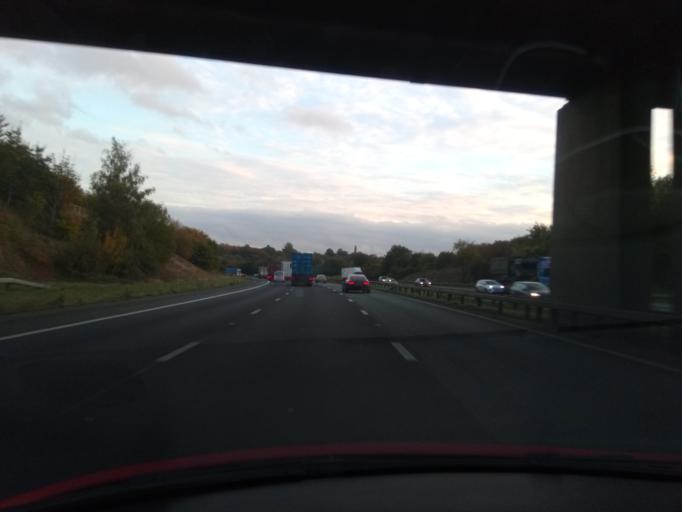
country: GB
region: England
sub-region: City and Borough of Leeds
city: Bramham
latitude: 53.8808
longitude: -1.3587
